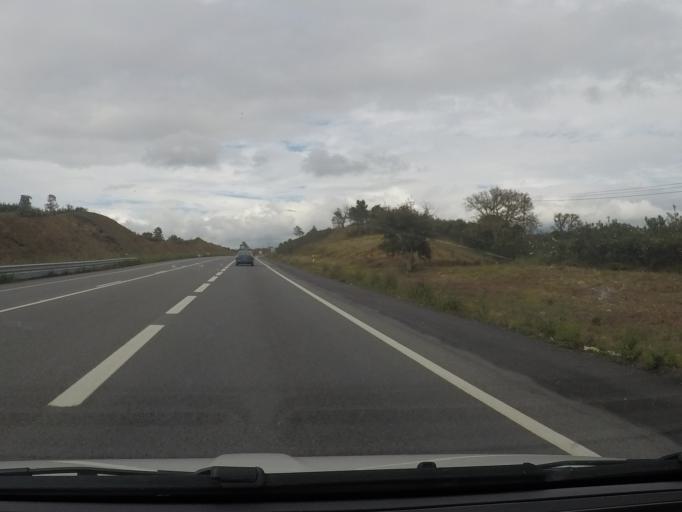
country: PT
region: Setubal
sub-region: Santiago do Cacem
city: Santiago do Cacem
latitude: 38.0649
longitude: -8.6997
